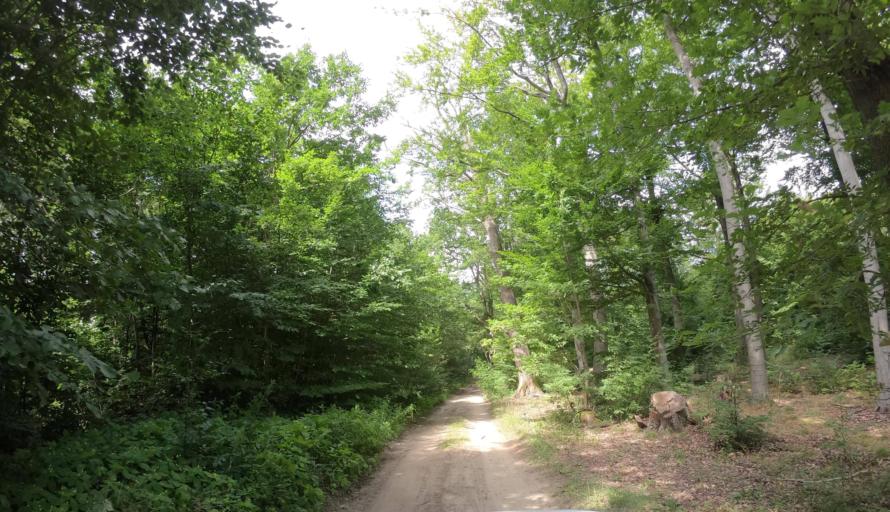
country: PL
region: West Pomeranian Voivodeship
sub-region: Powiat gryfinski
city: Stare Czarnowo
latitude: 53.3370
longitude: 14.8004
